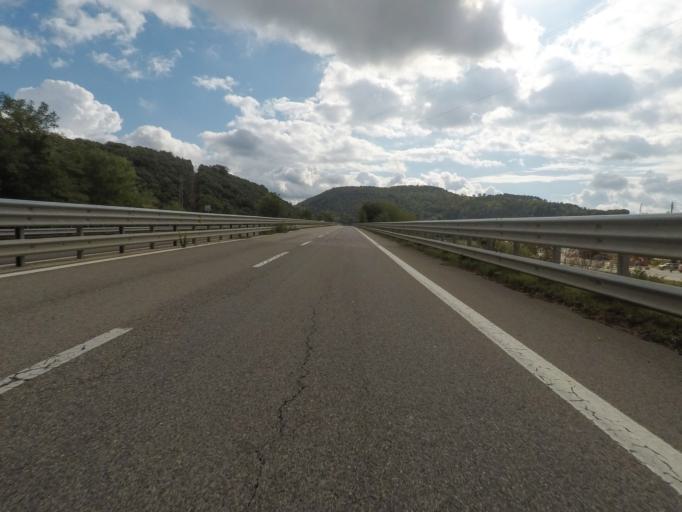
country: IT
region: Tuscany
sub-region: Provincia di Siena
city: Rapolano Terme
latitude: 43.2936
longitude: 11.6077
